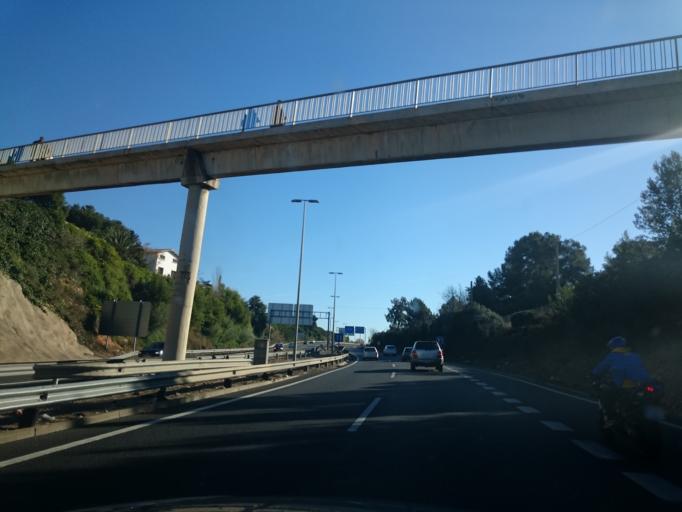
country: ES
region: Catalonia
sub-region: Provincia de Tarragona
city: Tarragona
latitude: 41.1246
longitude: 1.2467
